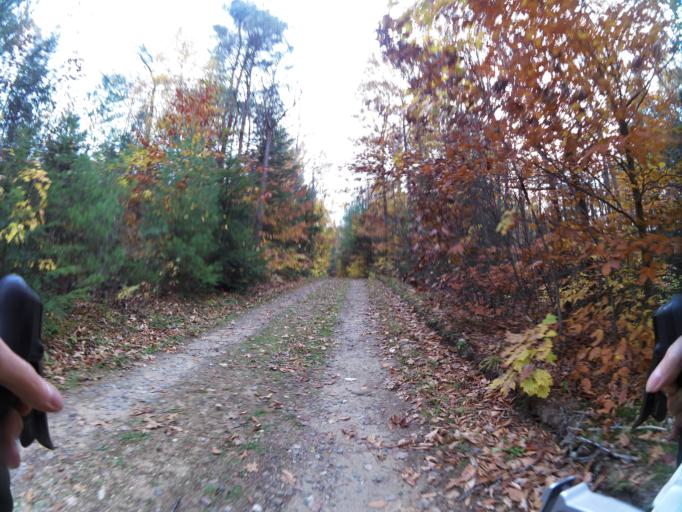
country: CA
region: Quebec
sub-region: Outaouais
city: Wakefield
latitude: 45.6144
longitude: -76.0132
